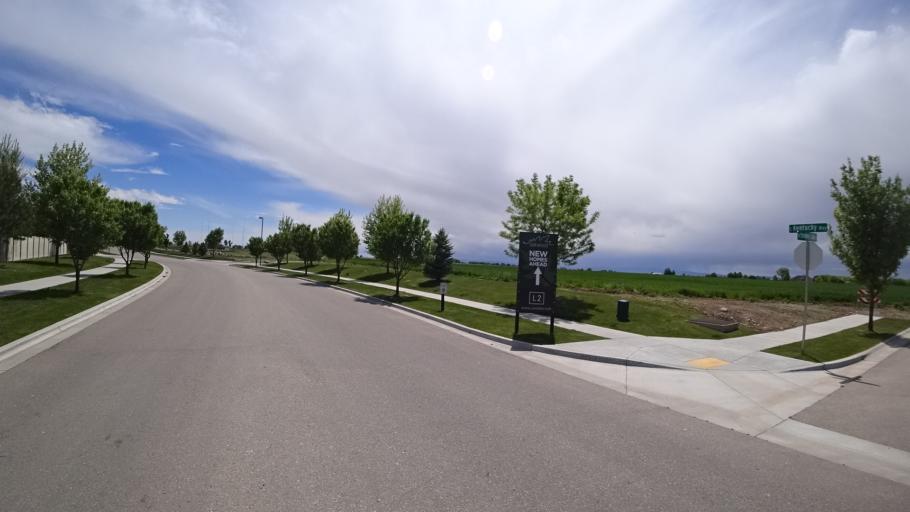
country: US
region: Idaho
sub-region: Ada County
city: Meridian
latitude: 43.5715
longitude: -116.4038
